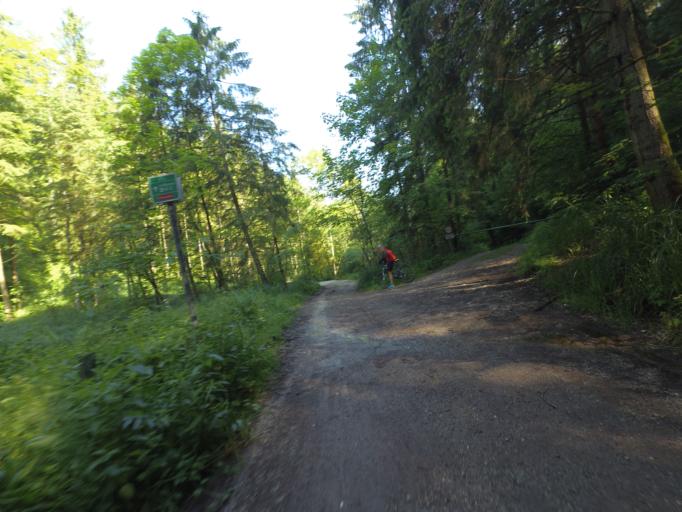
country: AT
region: Salzburg
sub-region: Politischer Bezirk Salzburg-Umgebung
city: Grodig
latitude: 47.7558
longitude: 12.9879
